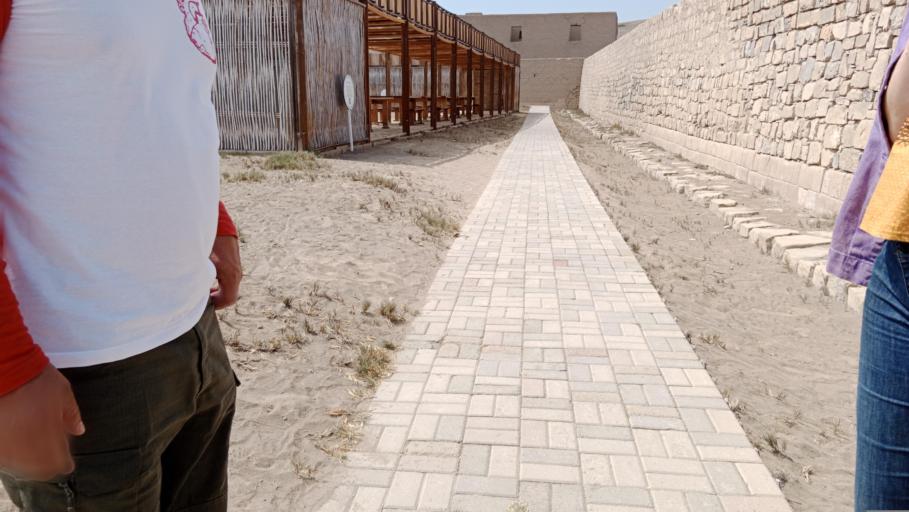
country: PE
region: Lima
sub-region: Lima
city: Punta Hermosa
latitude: -12.2571
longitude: -76.9049
